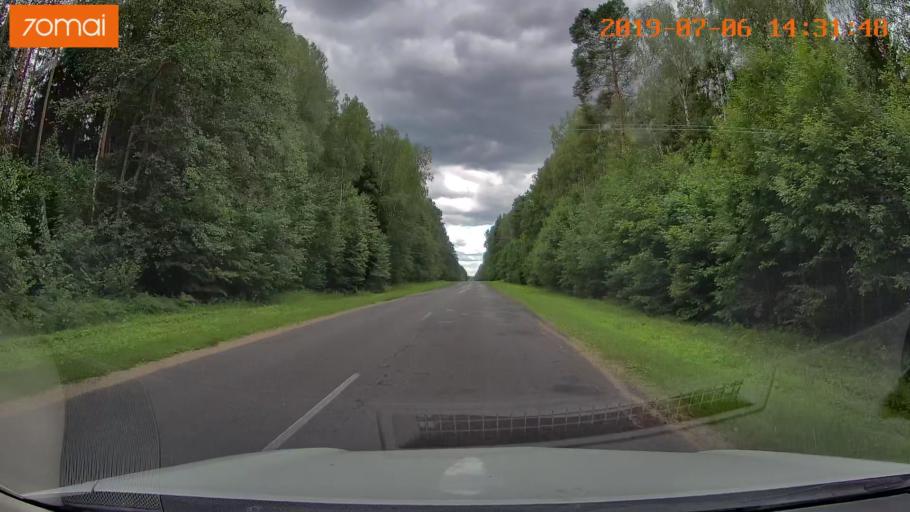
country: BY
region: Minsk
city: Ivyanyets
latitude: 53.9145
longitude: 26.7666
